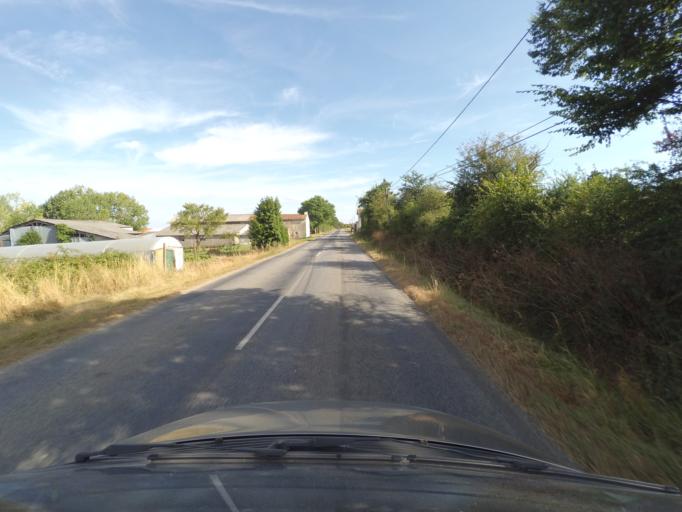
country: FR
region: Pays de la Loire
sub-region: Departement de la Loire-Atlantique
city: Vieillevigne
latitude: 46.9857
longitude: -1.4444
